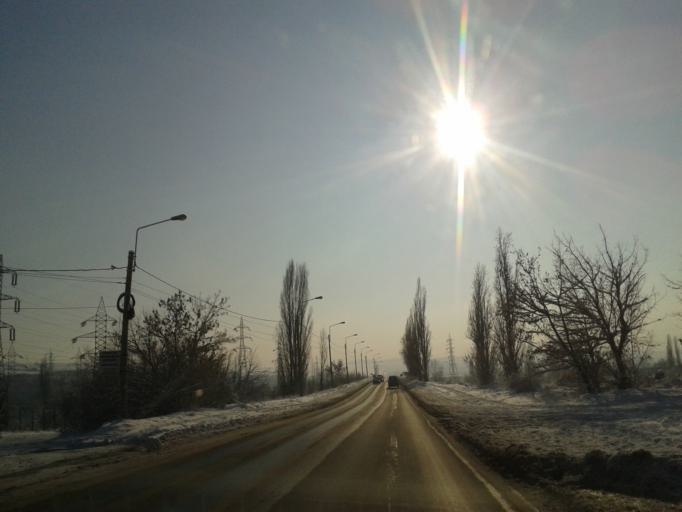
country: RO
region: Hunedoara
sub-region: Municipiul Hunedoara
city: Pestisu Mare
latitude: 45.7810
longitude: 22.9122
